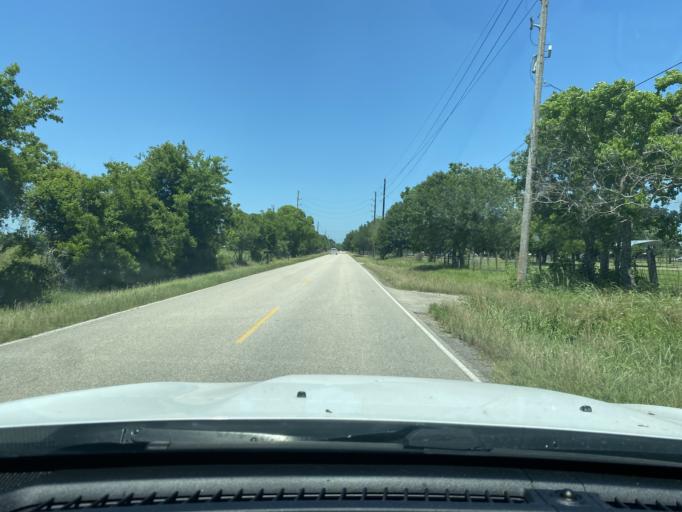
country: US
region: Texas
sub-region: Waller County
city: Waller
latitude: 30.0075
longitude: -95.8486
